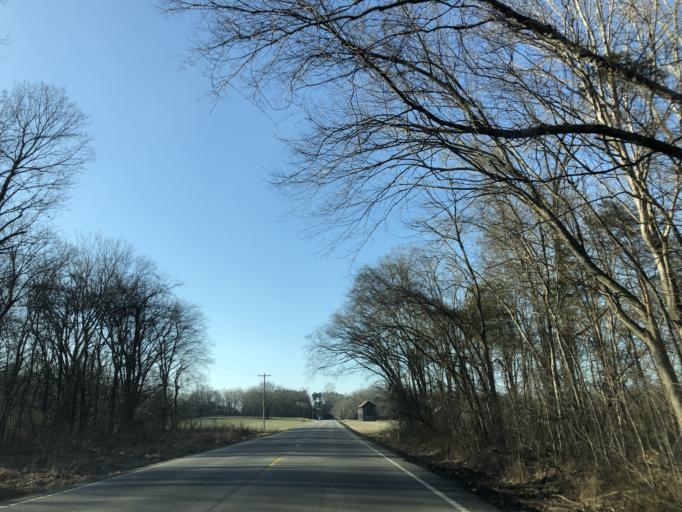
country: US
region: Tennessee
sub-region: Sumner County
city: White House
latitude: 36.5244
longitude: -86.6307
